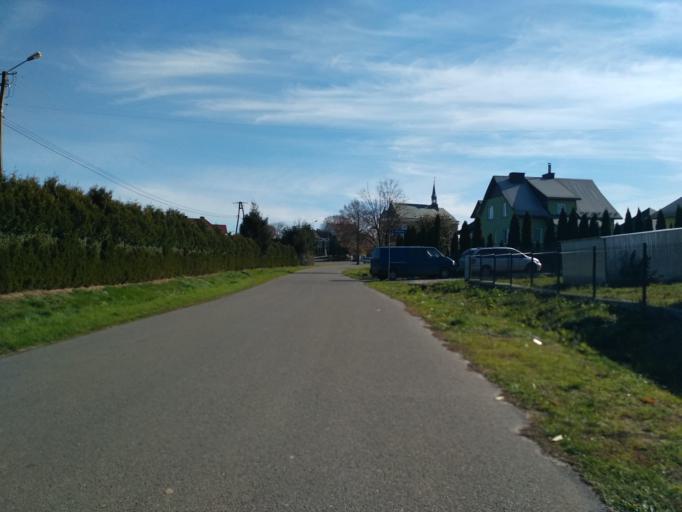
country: PL
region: Subcarpathian Voivodeship
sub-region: Powiat ropczycko-sedziszowski
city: Iwierzyce
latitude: 50.0610
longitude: 21.7842
